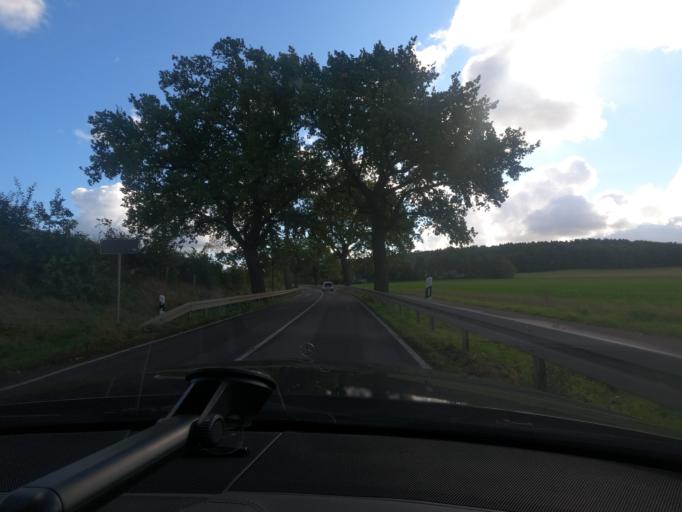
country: DE
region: Brandenburg
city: Potsdam
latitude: 52.4565
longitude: 13.0393
